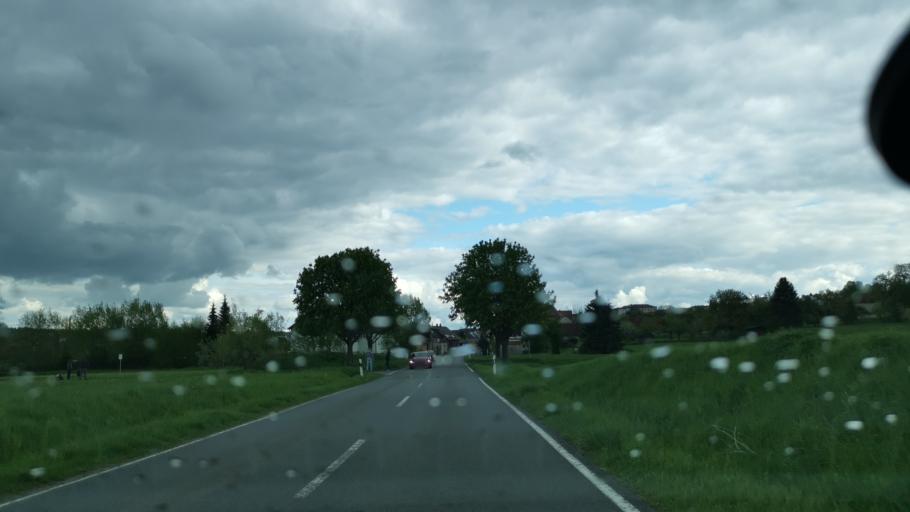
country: DE
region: Baden-Wuerttemberg
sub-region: Karlsruhe Region
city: Buchen
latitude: 49.5007
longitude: 9.3903
